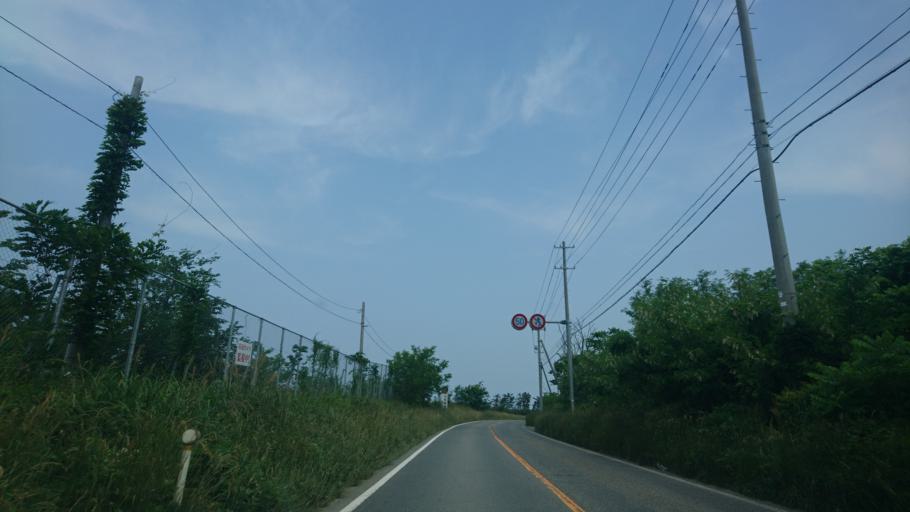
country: JP
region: Niigata
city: Shibata
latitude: 38.0260
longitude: 139.2874
